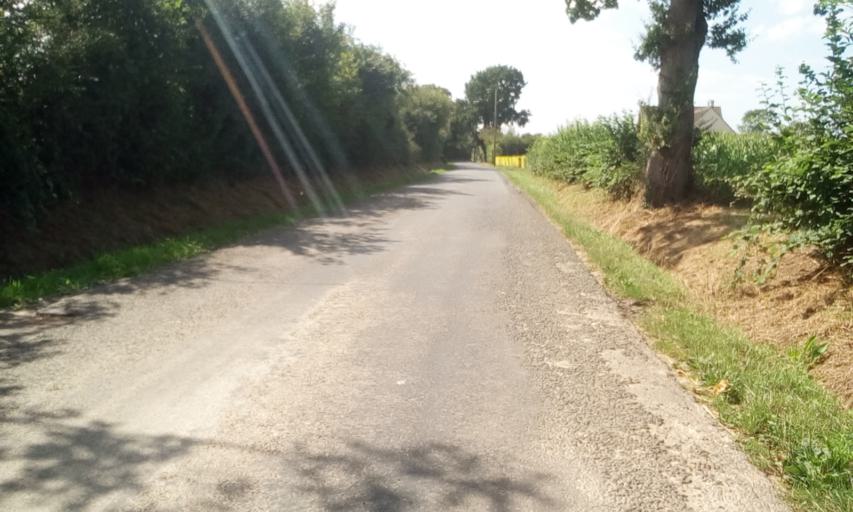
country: FR
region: Lower Normandy
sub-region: Departement du Calvados
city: Argences
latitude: 49.1536
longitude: -0.1404
